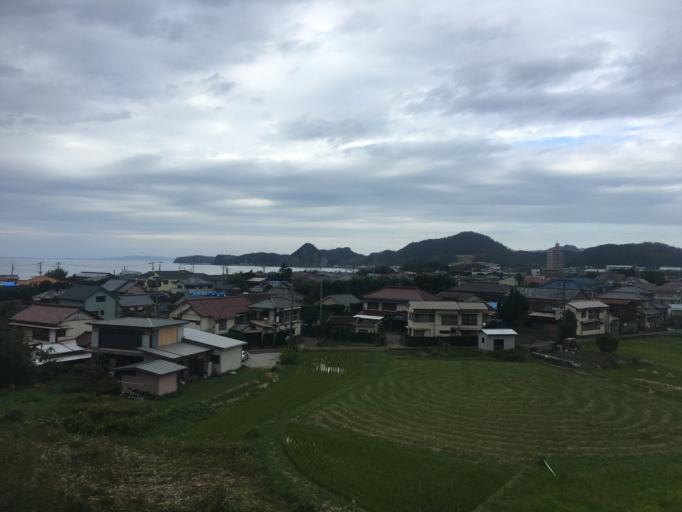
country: JP
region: Chiba
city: Tateyama
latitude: 35.0827
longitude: 139.8457
